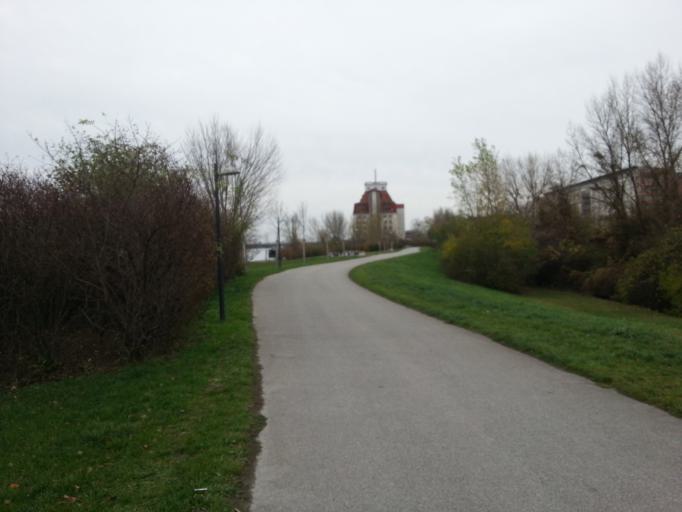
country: AT
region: Vienna
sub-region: Wien Stadt
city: Vienna
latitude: 48.2166
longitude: 16.4182
